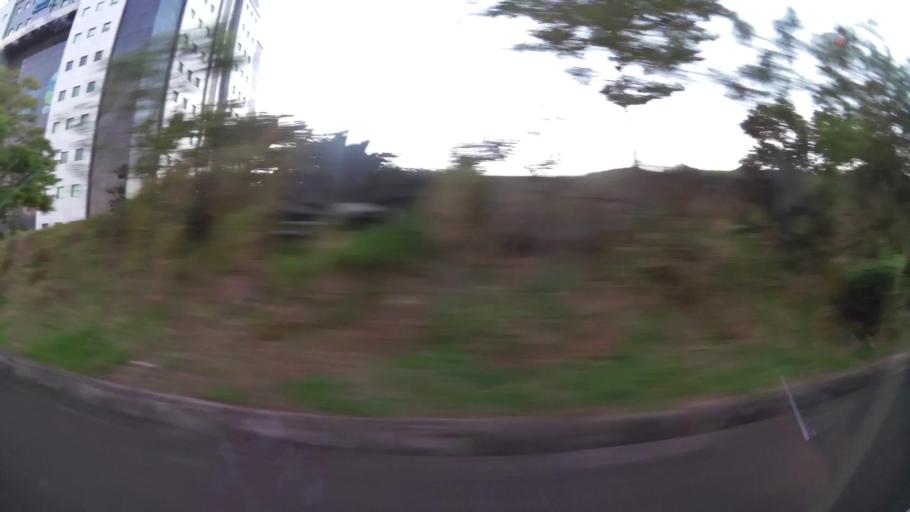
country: MU
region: Plaines Wilhems
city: Ebene
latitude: -20.2428
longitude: 57.4970
